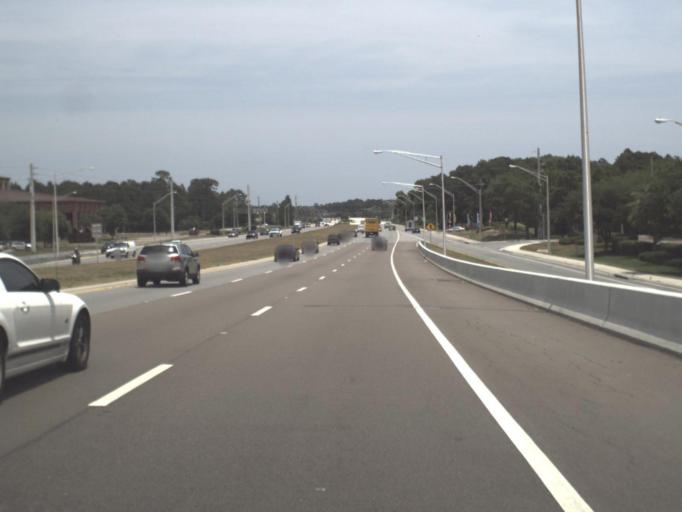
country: US
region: Florida
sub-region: Duval County
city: Atlantic Beach
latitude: 30.3190
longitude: -81.4873
